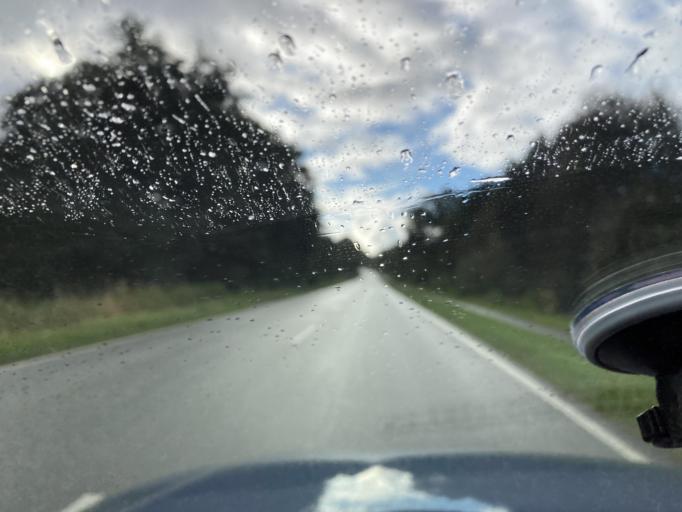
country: DE
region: Schleswig-Holstein
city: Tellingstedt
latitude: 54.2196
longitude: 9.3127
